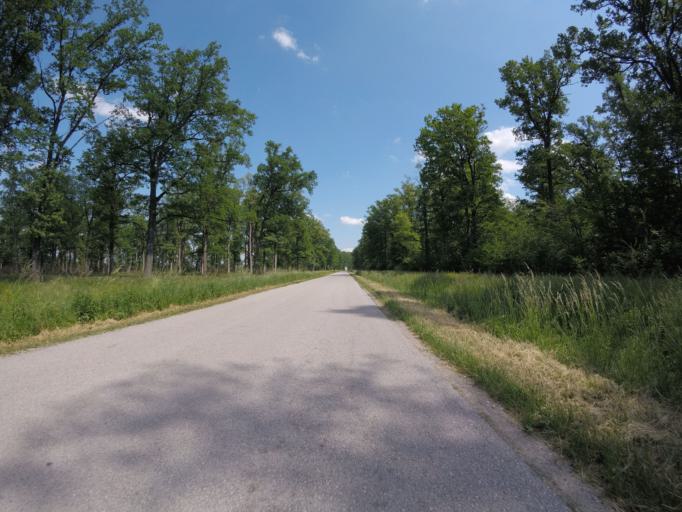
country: HR
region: Zagrebacka
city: Kuce
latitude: 45.6752
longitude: 16.1690
